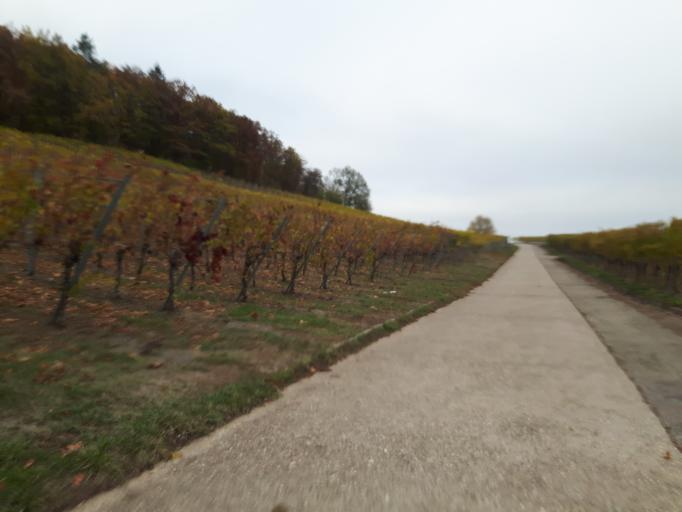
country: DE
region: Baden-Wuerttemberg
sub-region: Karlsruhe Region
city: Zaisenhausen
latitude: 49.1679
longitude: 8.8257
